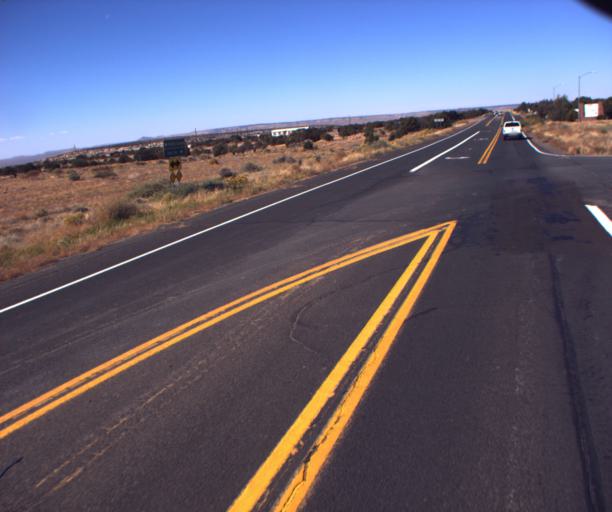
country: US
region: Arizona
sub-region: Navajo County
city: First Mesa
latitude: 35.8425
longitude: -110.5283
